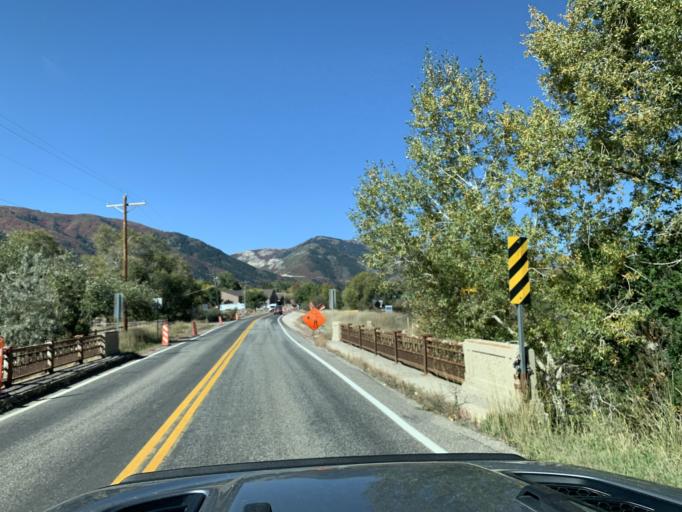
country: US
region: Utah
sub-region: Weber County
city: Wolf Creek
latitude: 41.3135
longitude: -111.8408
